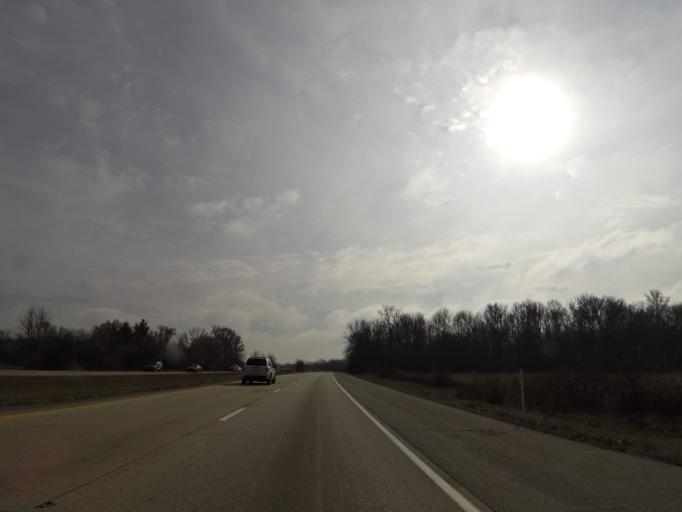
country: US
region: Indiana
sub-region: Shelby County
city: Shelbyville
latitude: 39.6079
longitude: -85.8554
